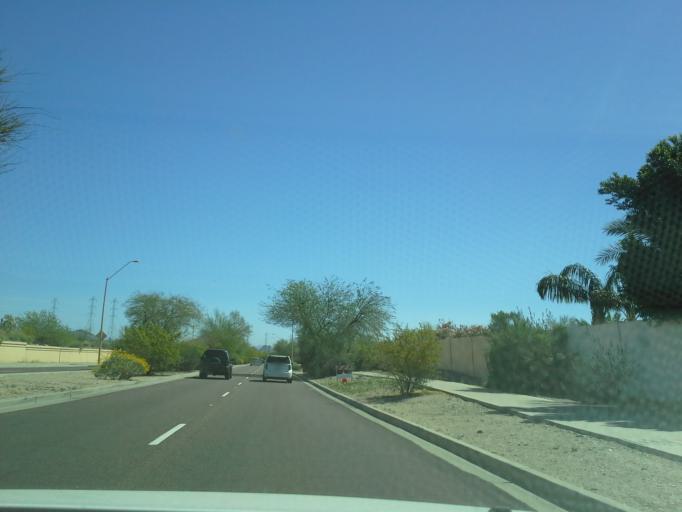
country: US
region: Arizona
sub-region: Maricopa County
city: Scottsdale
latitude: 33.6026
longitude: -111.8530
